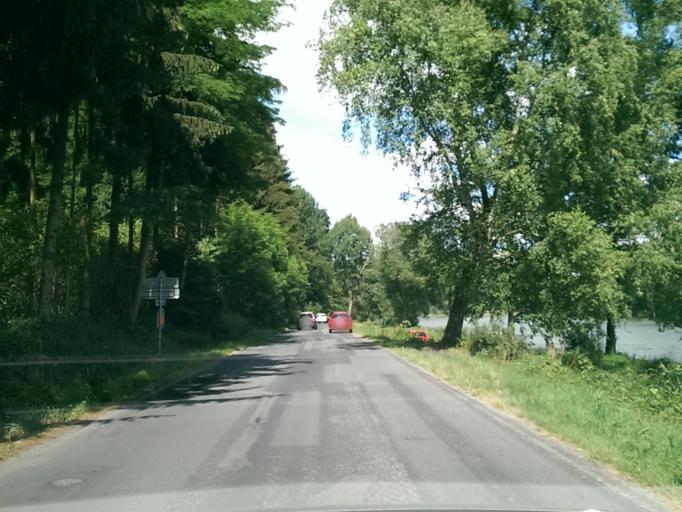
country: CZ
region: Central Bohemia
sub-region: Okres Melnik
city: Melnik
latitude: 50.3888
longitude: 14.5430
